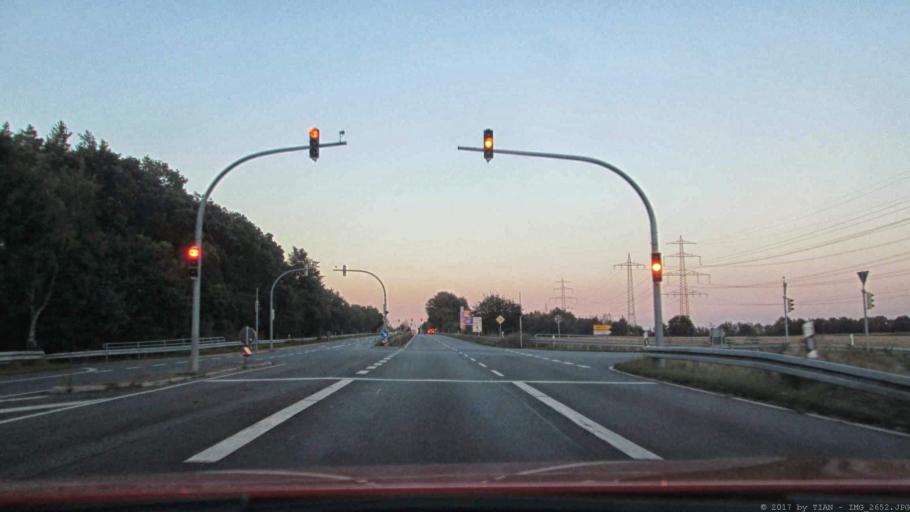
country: DE
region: Lower Saxony
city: Lehre
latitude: 52.3665
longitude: 10.7177
